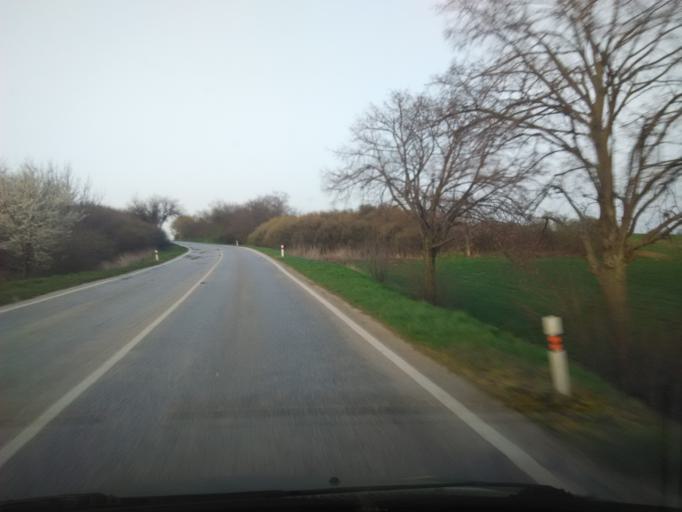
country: SK
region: Nitriansky
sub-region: Okres Nitra
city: Nitra
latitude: 48.2392
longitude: 18.0127
